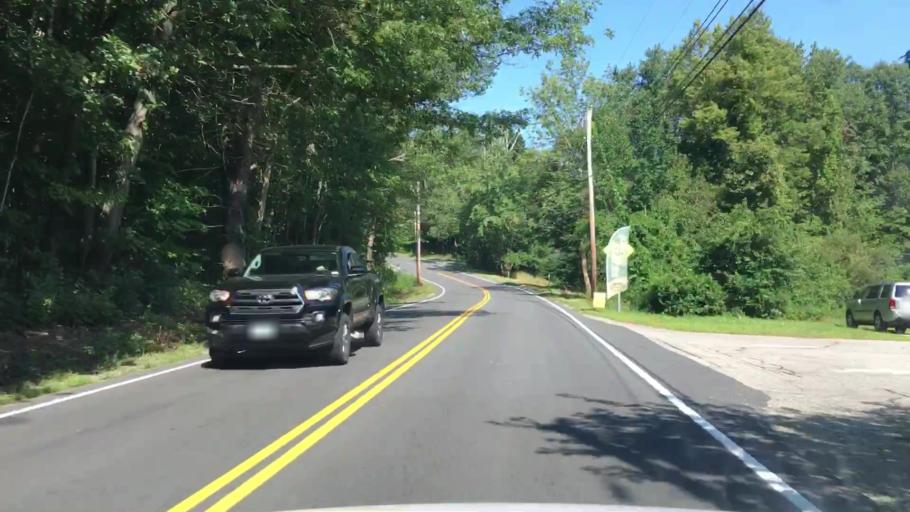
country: US
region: New Hampshire
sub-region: Rockingham County
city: Kensington
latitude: 42.9118
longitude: -70.9634
